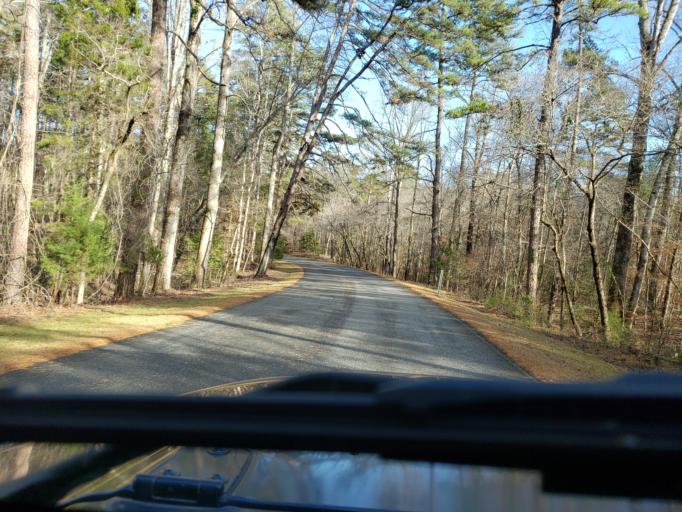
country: US
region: North Carolina
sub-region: Cleveland County
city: Kings Mountain
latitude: 35.1400
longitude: -81.3476
